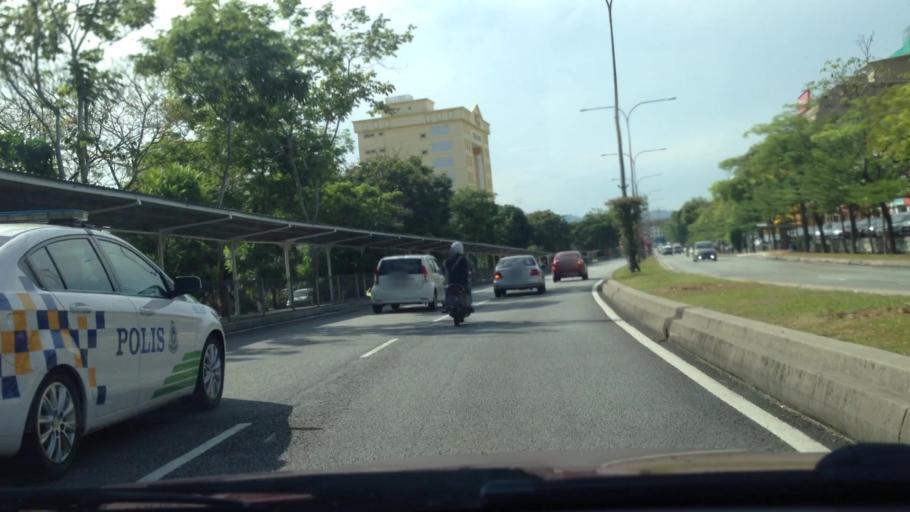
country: MY
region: Selangor
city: Subang Jaya
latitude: 3.0502
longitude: 101.5851
